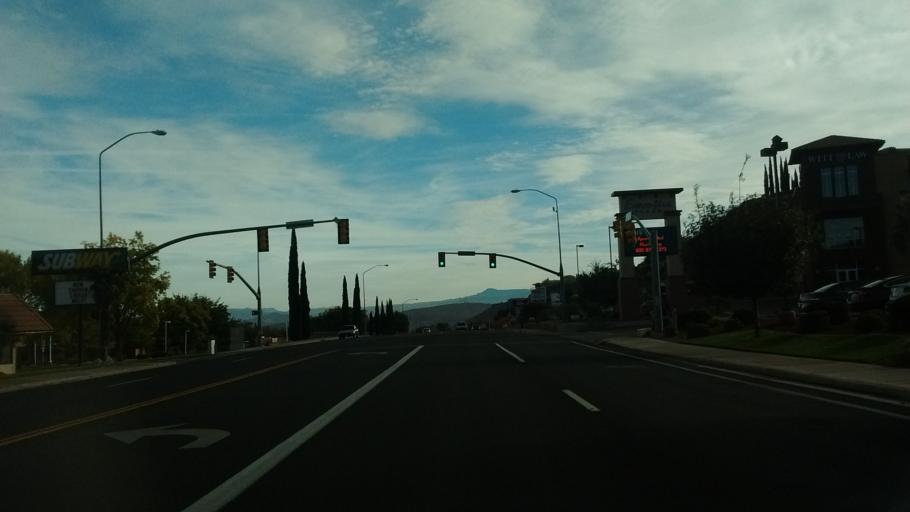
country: US
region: Utah
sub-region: Washington County
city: Saint George
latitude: 37.1172
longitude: -113.5971
